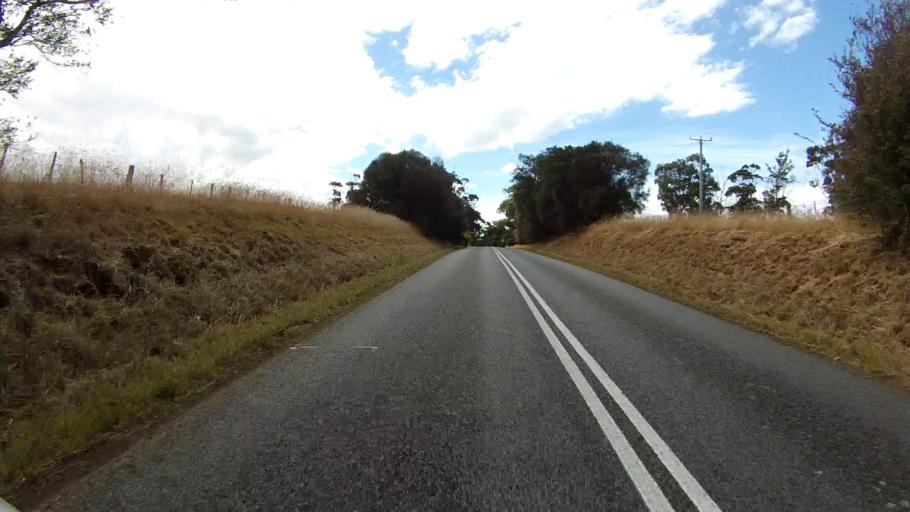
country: AU
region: Tasmania
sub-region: Sorell
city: Sorell
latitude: -42.2592
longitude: 148.0033
